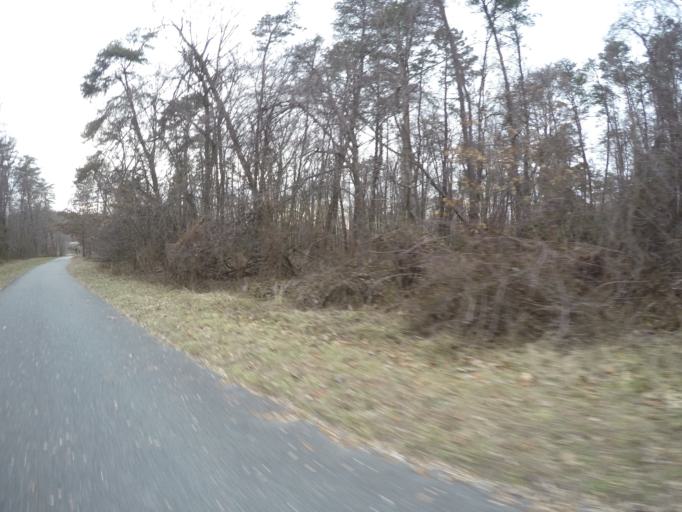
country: US
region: Maryland
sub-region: Howard County
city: Elkridge
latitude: 39.1922
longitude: -76.6890
